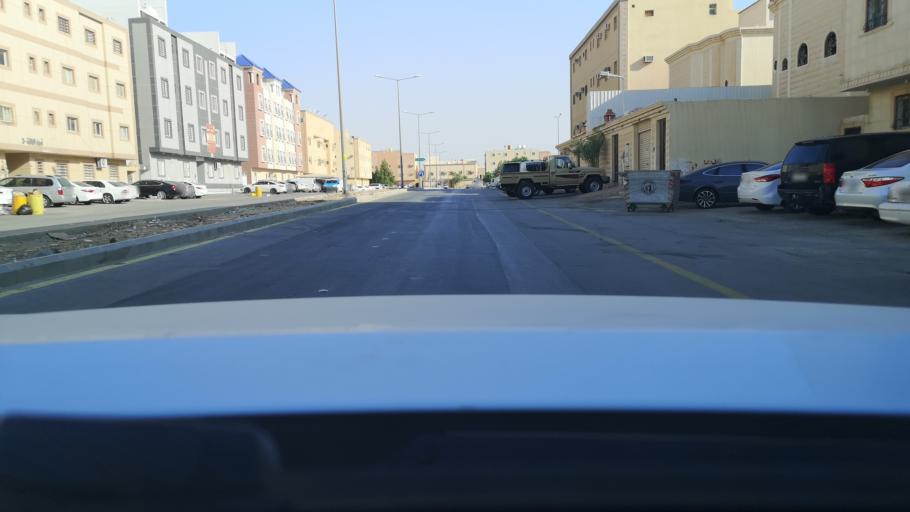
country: SA
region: Ar Riyad
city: Riyadh
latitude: 24.6388
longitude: 46.5537
